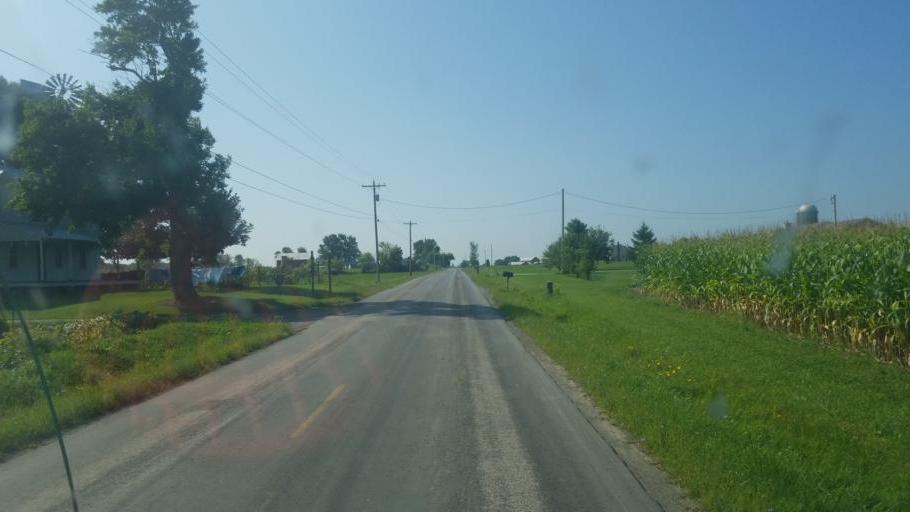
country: US
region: Ohio
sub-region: Wayne County
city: West Salem
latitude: 41.0119
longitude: -82.1639
